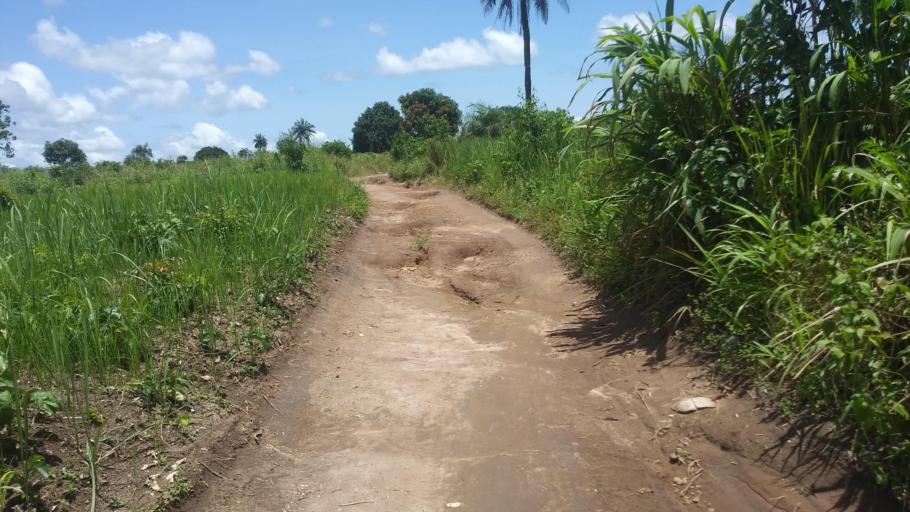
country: SL
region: Northern Province
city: Makeni
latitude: 8.8868
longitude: -12.0153
